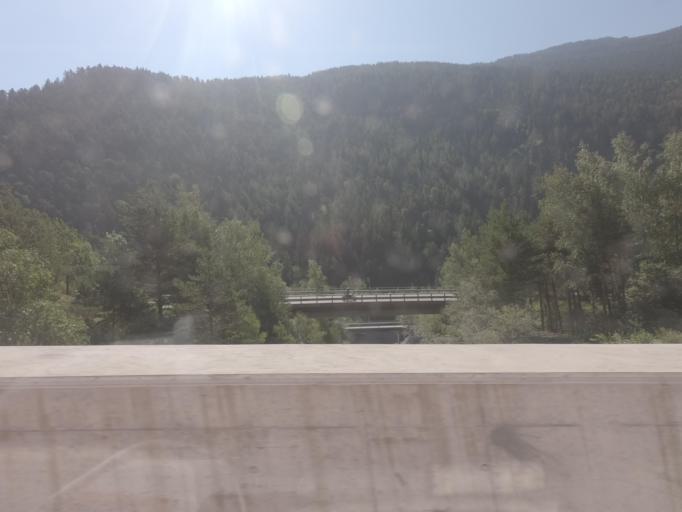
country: CH
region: Valais
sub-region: Entremont District
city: Bagnes
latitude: 46.0833
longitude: 7.1822
